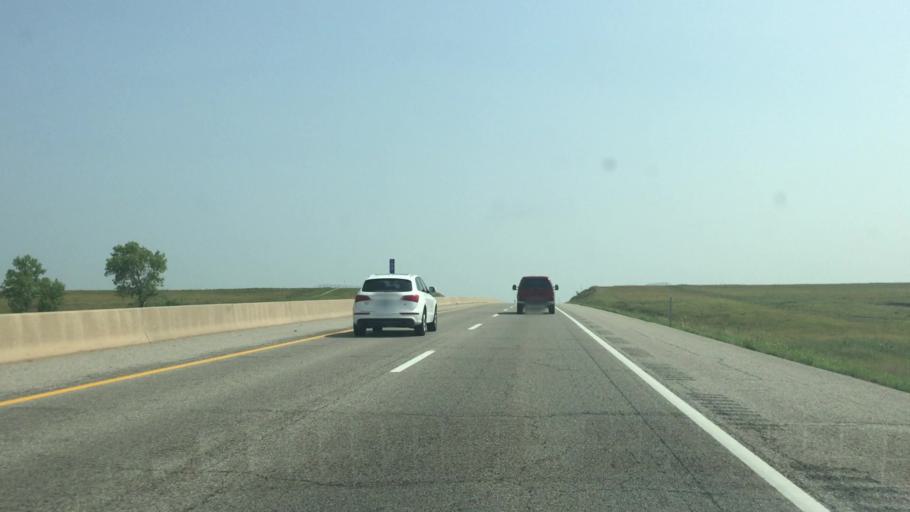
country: US
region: Kansas
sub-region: Lyon County
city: Emporia
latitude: 38.3199
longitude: -96.3241
